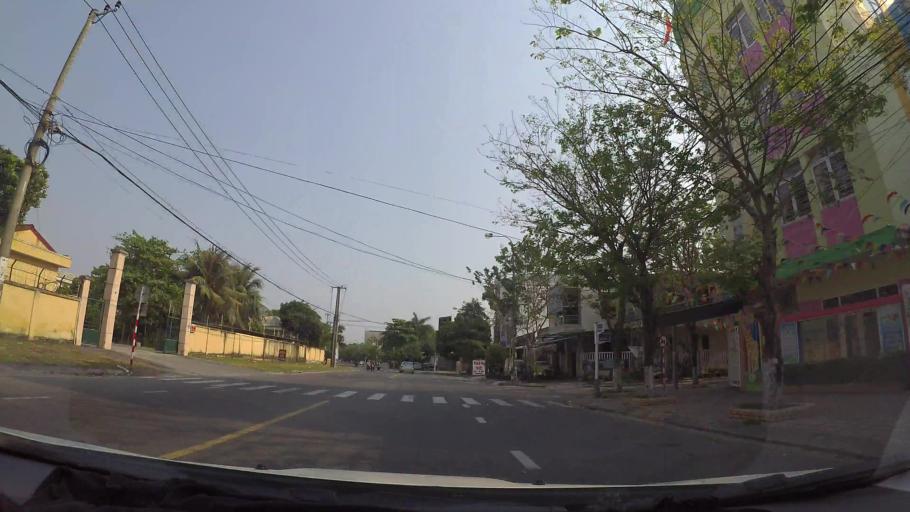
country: VN
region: Da Nang
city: Cam Le
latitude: 16.0172
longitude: 108.1986
